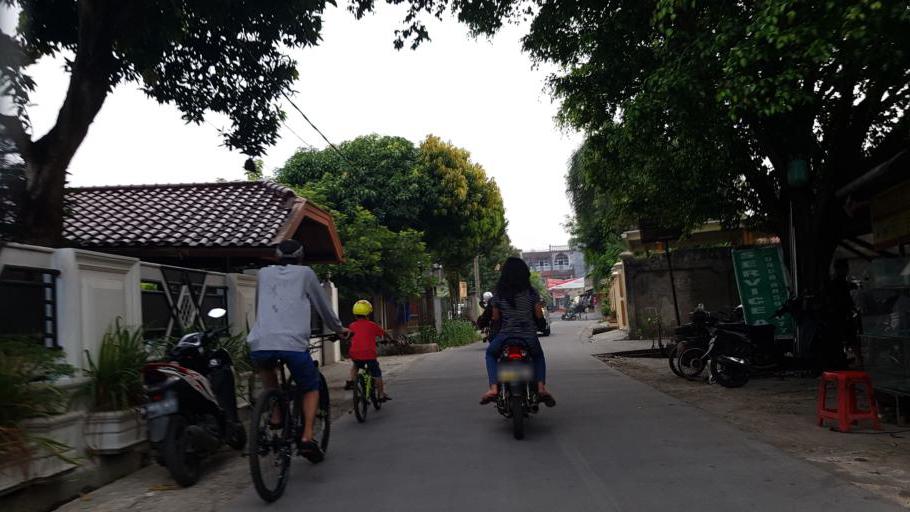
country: ID
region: West Java
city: Depok
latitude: -6.3799
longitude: 106.8057
